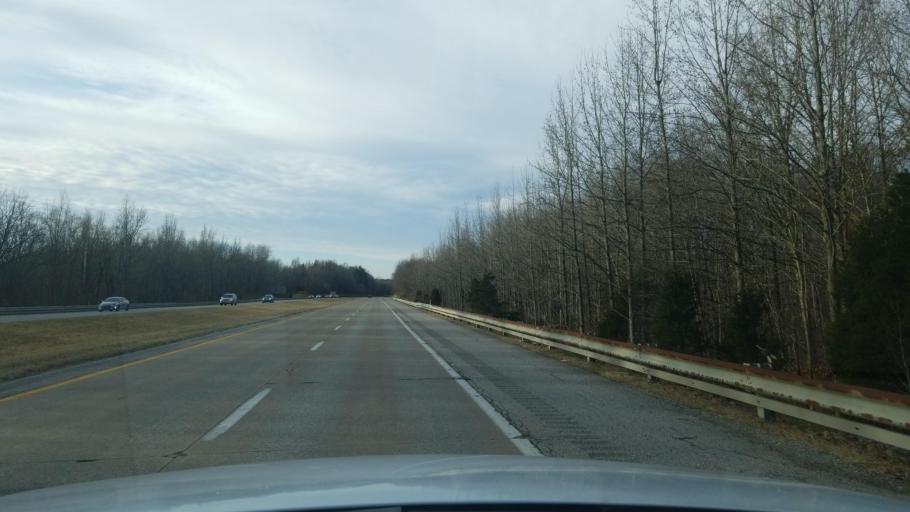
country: US
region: Indiana
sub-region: Vanderburgh County
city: Evansville
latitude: 37.9585
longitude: -87.6932
